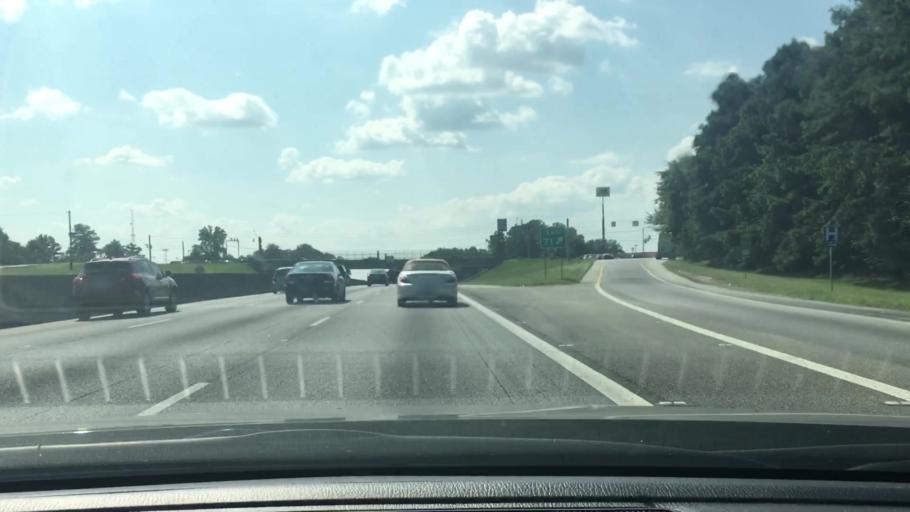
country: US
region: Georgia
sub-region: DeKalb County
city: Redan
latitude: 33.7027
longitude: -84.1673
